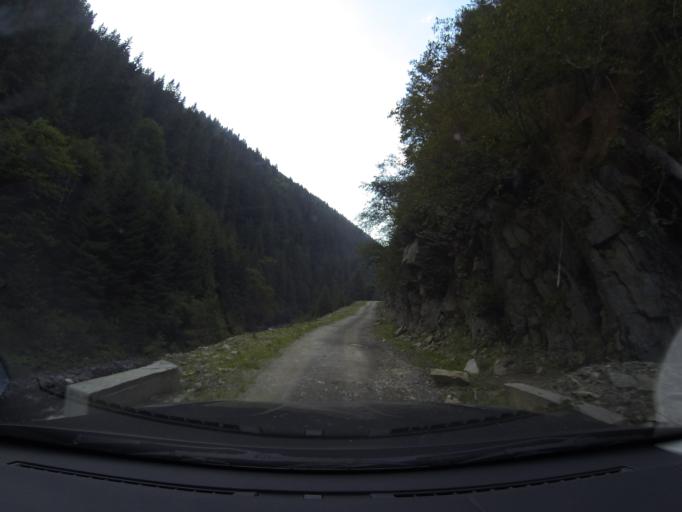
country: RO
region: Brasov
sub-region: Oras Victoria
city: Victoria
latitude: 45.5485
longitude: 24.6803
